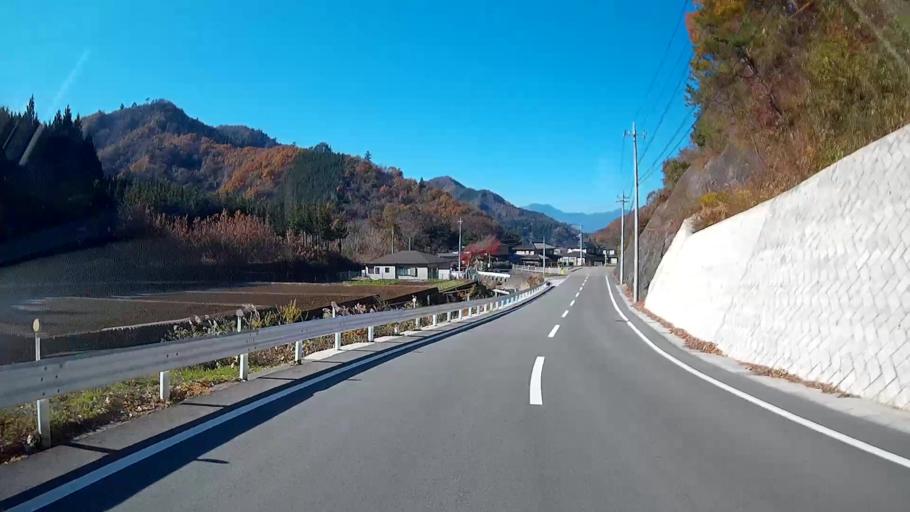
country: JP
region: Yamanashi
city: Otsuki
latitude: 35.5607
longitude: 138.9922
